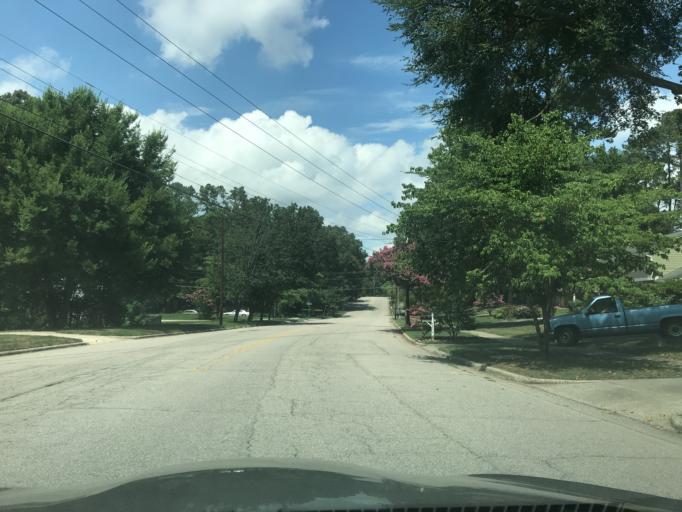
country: US
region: North Carolina
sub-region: Wake County
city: West Raleigh
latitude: 35.8459
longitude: -78.6235
